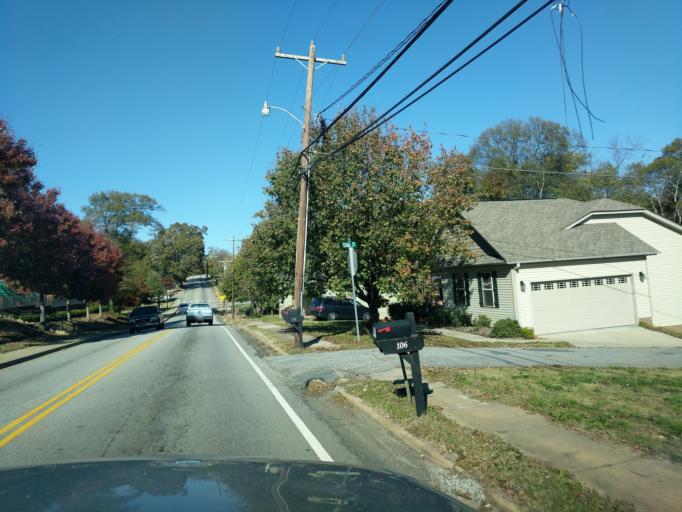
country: US
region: South Carolina
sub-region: Greenville County
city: Greer
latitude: 34.9374
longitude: -82.2223
